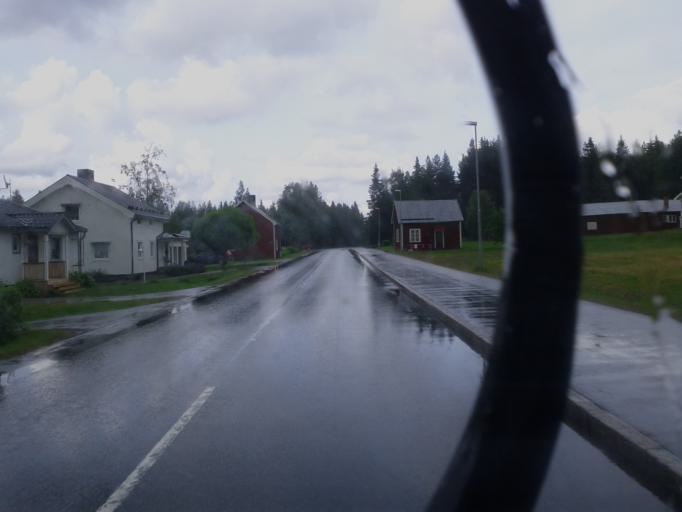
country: SE
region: Vaesterbotten
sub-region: Mala Kommun
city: Mala
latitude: 65.0878
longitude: 18.9555
